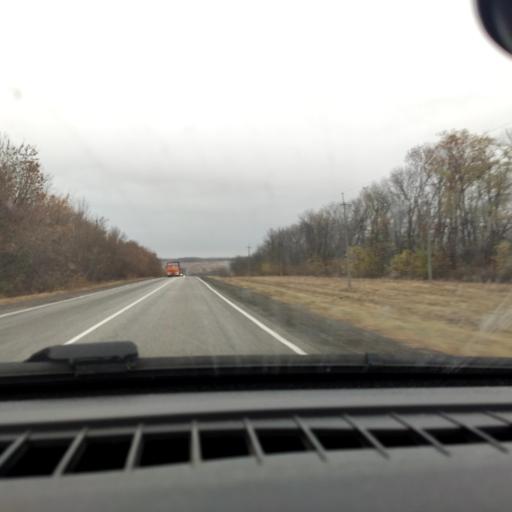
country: RU
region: Voronezj
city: Uryv-Pokrovka
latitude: 51.1124
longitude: 39.0269
